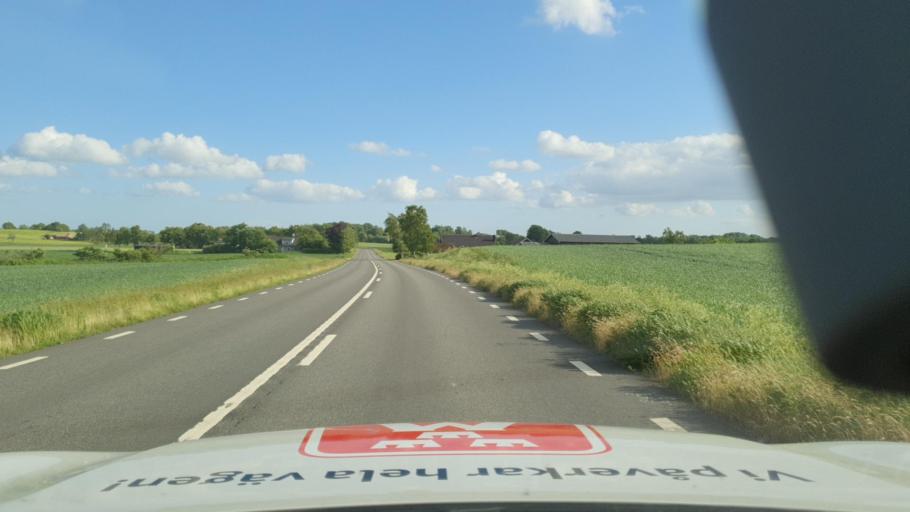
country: SE
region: Skane
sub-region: Simrishamns Kommun
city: Kivik
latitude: 55.5877
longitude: 14.1242
